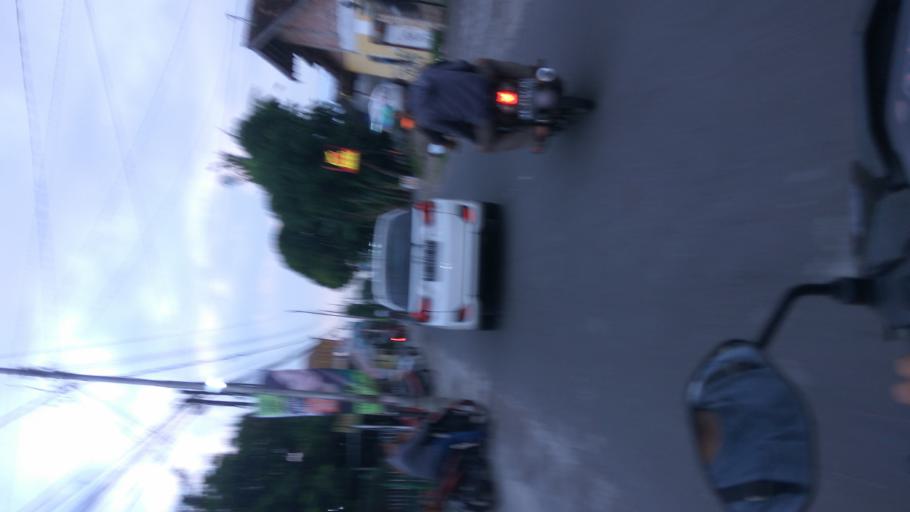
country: ID
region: Daerah Istimewa Yogyakarta
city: Depok
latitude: -7.7530
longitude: 110.3999
